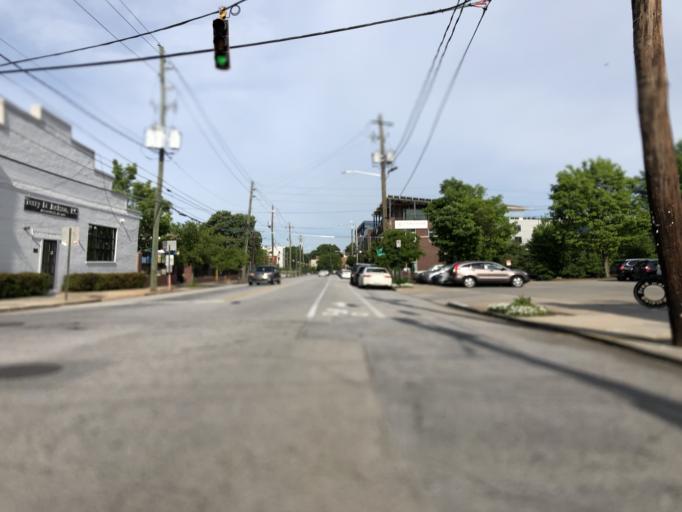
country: US
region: Georgia
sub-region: Fulton County
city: Atlanta
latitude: 33.7543
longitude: -84.3681
